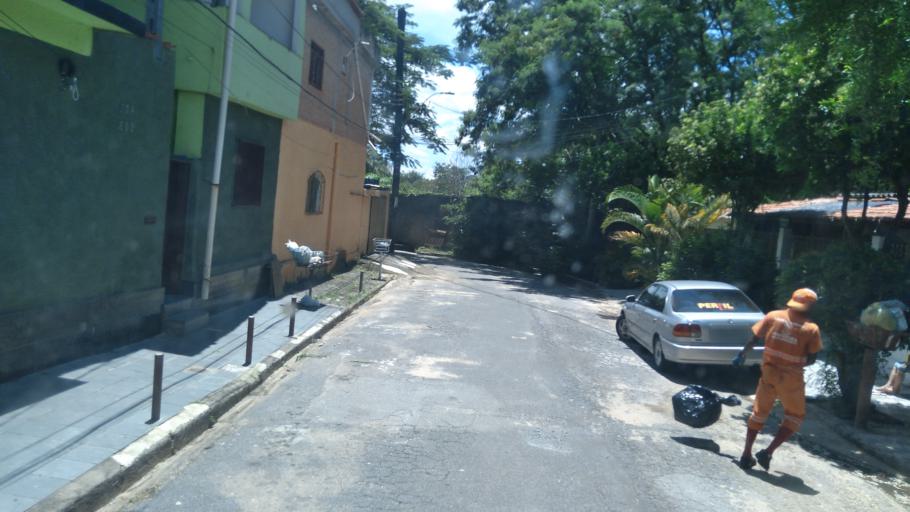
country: BR
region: Minas Gerais
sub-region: Belo Horizonte
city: Belo Horizonte
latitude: -19.8611
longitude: -43.8960
